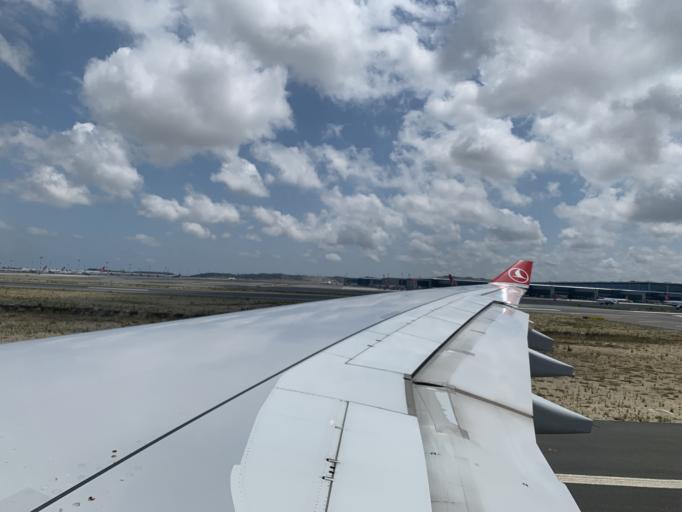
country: TR
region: Istanbul
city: Durusu
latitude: 41.2680
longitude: 28.7254
